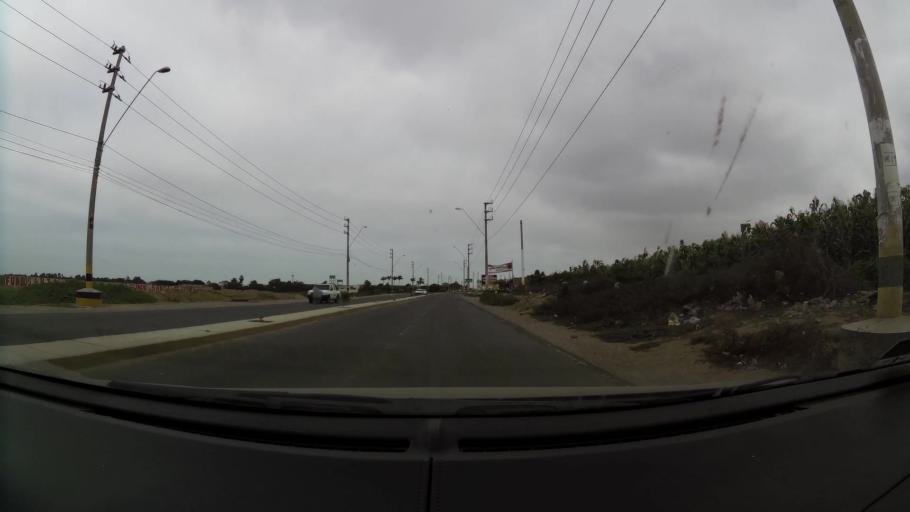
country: PE
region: La Libertad
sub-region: Provincia de Trujillo
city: Huanchaco
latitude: -8.0924
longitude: -79.0802
